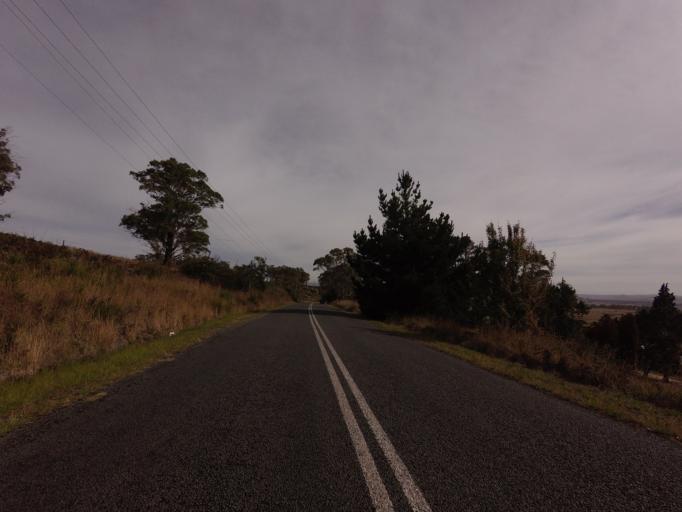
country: AU
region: Tasmania
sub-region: Brighton
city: Bridgewater
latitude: -42.3783
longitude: 147.4244
